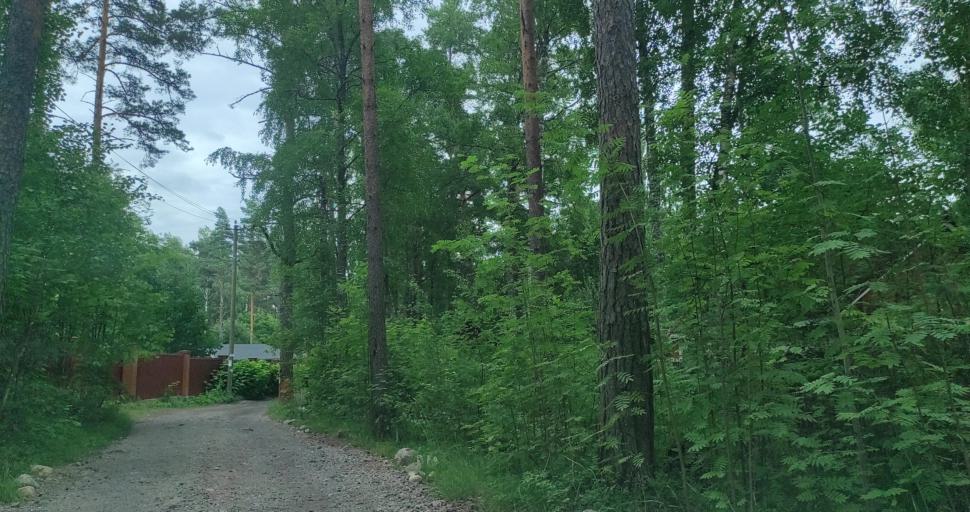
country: RU
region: Leningrad
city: Sapernoye
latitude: 60.6818
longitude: 29.9809
